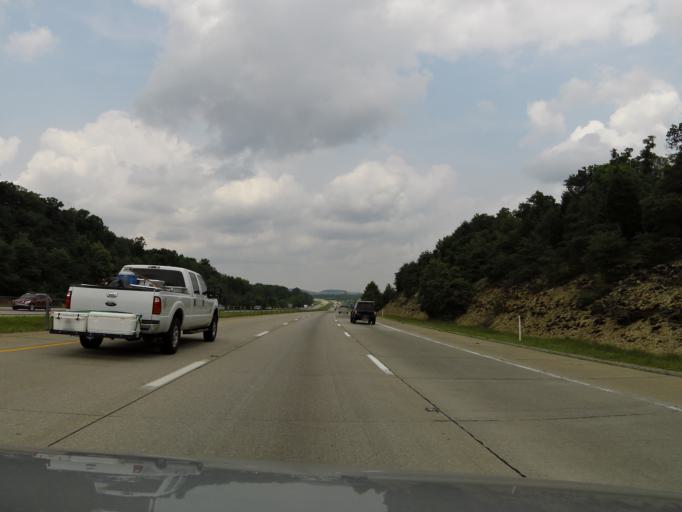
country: US
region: Kentucky
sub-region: Bullitt County
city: Shepherdsville
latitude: 37.9608
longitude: -85.6938
